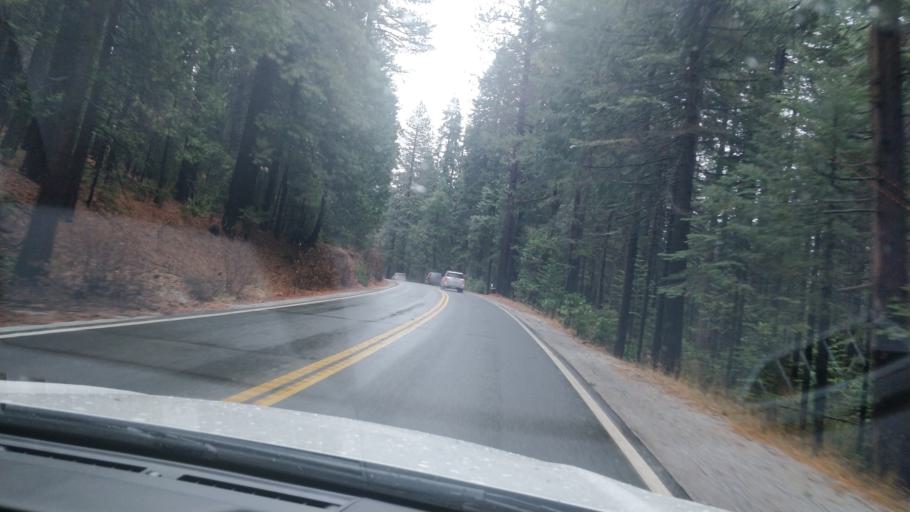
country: US
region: California
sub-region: Nevada County
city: Nevada City
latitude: 39.3211
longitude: -120.8288
